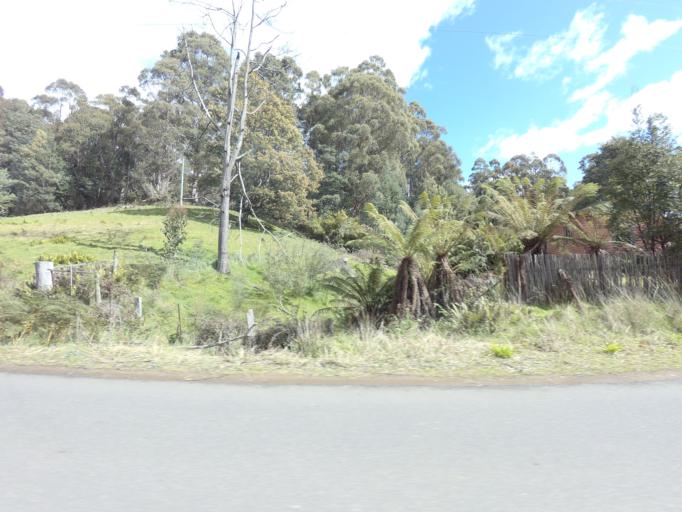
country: AU
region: Tasmania
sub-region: Huon Valley
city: Geeveston
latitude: -43.4171
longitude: 146.9649
